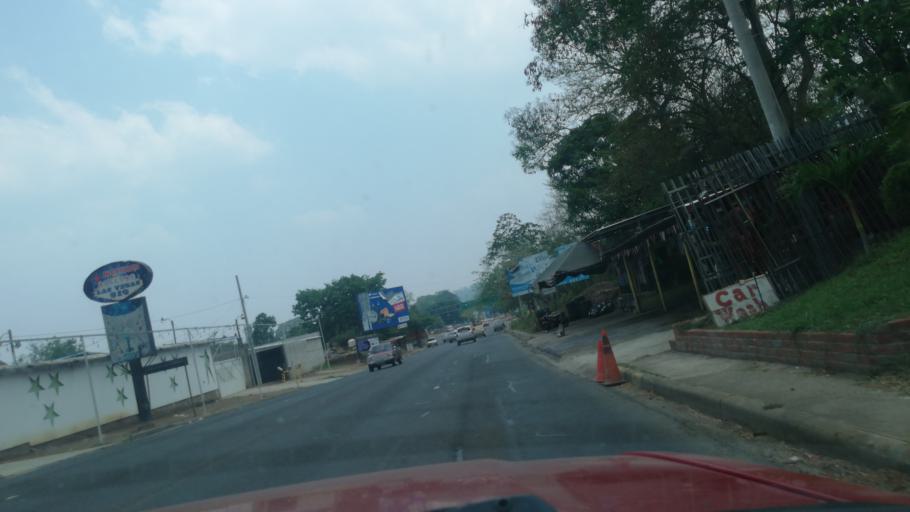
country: SV
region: Santa Ana
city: Santa Ana
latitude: 13.9818
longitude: -89.5962
